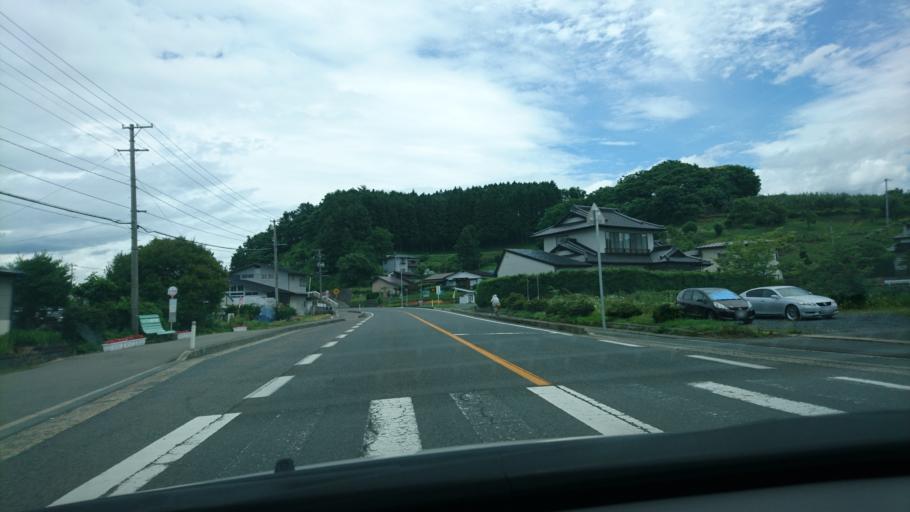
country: JP
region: Iwate
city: Morioka-shi
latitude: 39.6317
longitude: 141.1841
